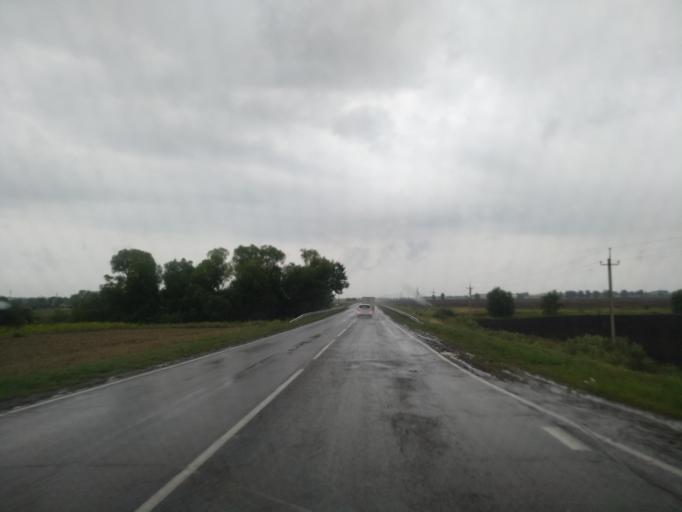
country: RU
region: Voronezj
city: Verkhnyaya Khava
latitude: 51.6778
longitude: 39.8582
